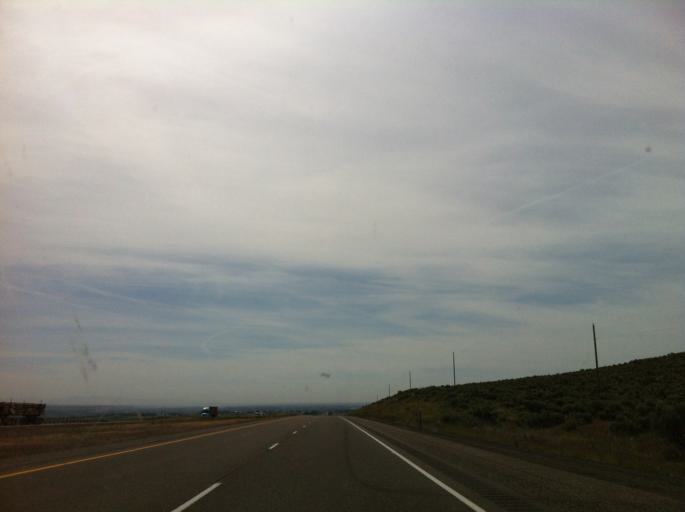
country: US
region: Oregon
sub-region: Malheur County
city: Ontario
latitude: 44.1140
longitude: -117.0598
